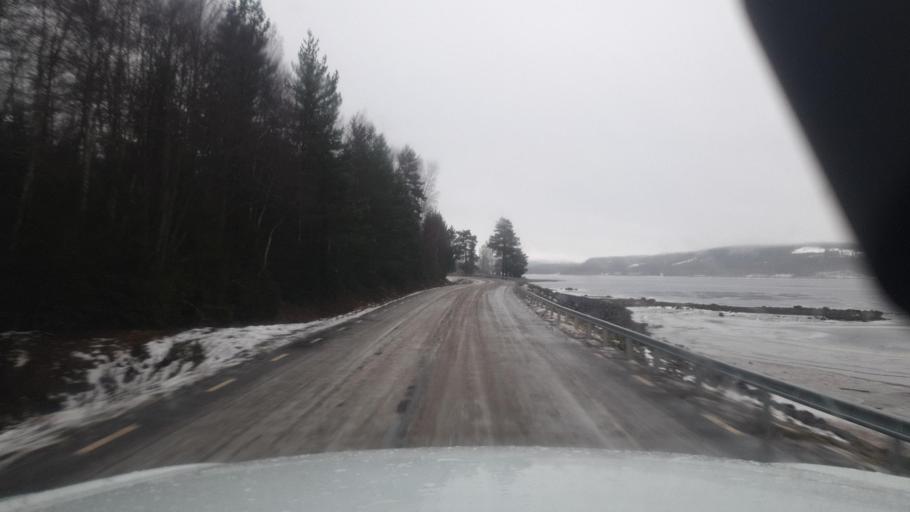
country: SE
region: Vaermland
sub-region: Torsby Kommun
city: Torsby
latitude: 59.9858
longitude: 12.7866
